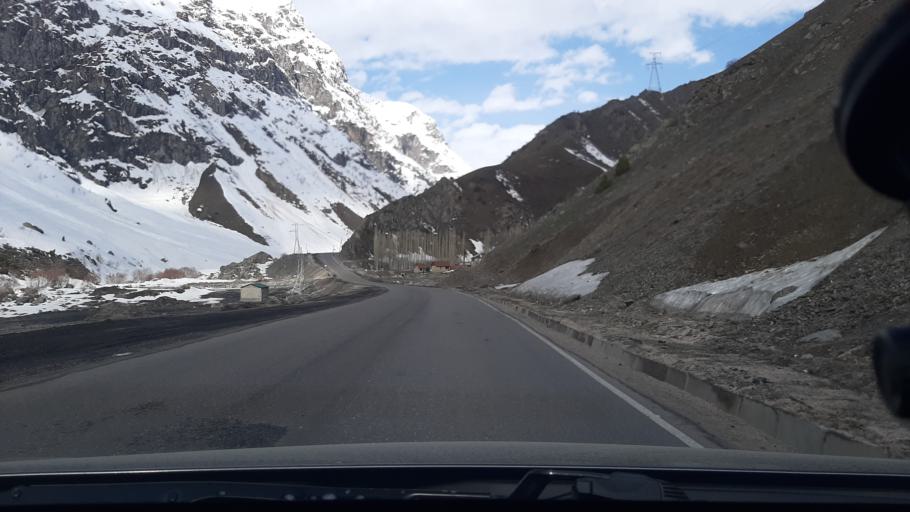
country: TJ
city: Tagob
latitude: 39.0362
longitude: 68.7712
